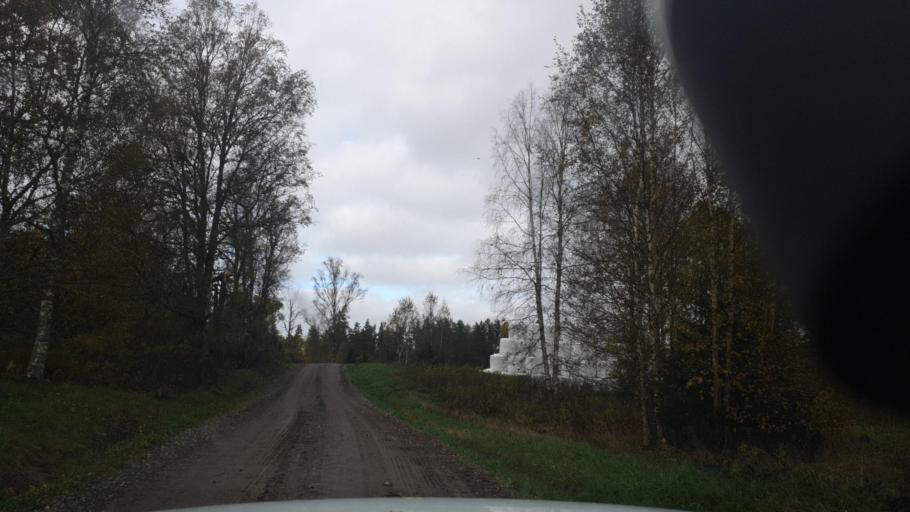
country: SE
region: Vaermland
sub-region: Karlstads Kommun
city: Edsvalla
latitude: 59.4719
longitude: 13.1275
